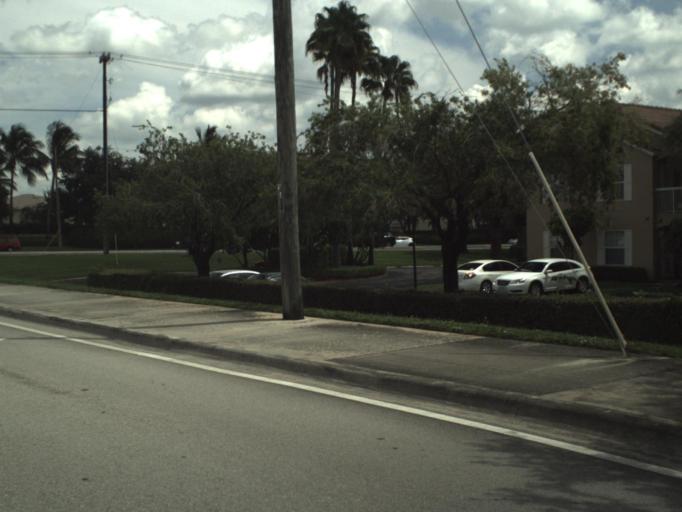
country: US
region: Florida
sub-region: Palm Beach County
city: North Palm Beach
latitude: 26.8298
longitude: -80.0913
